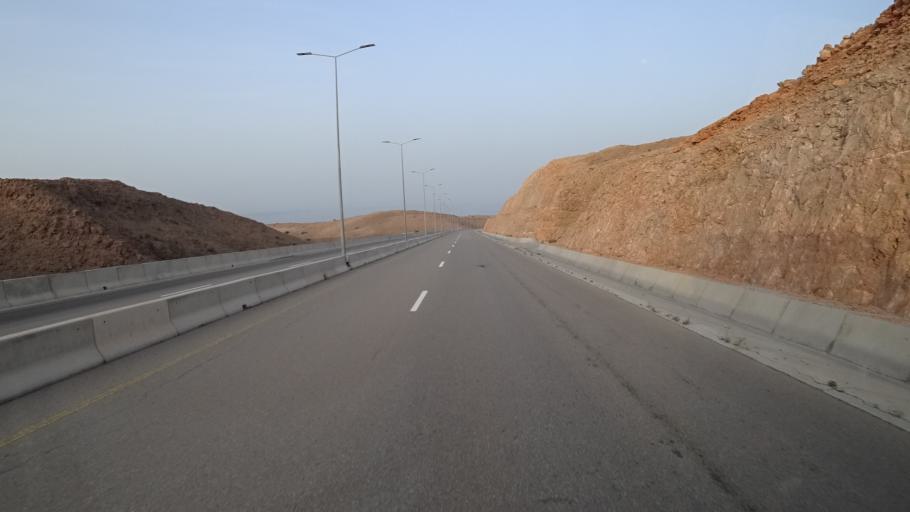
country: OM
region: Ash Sharqiyah
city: Al Qabil
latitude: 23.0921
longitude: 59.0110
